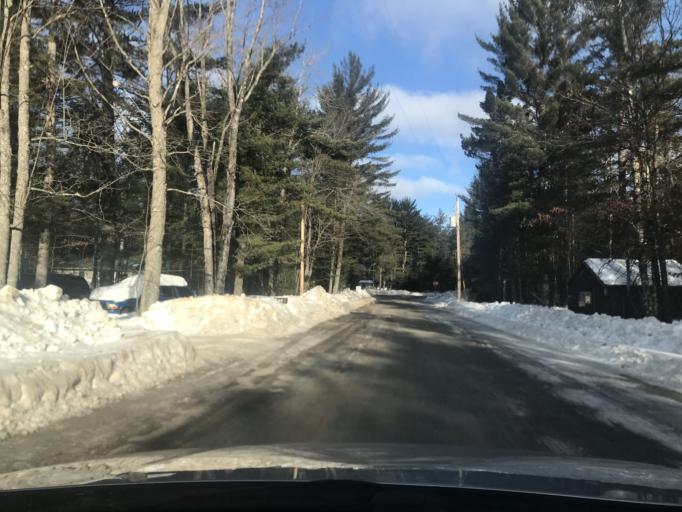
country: US
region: Wisconsin
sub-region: Marinette County
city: Niagara
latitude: 45.6369
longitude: -87.9702
